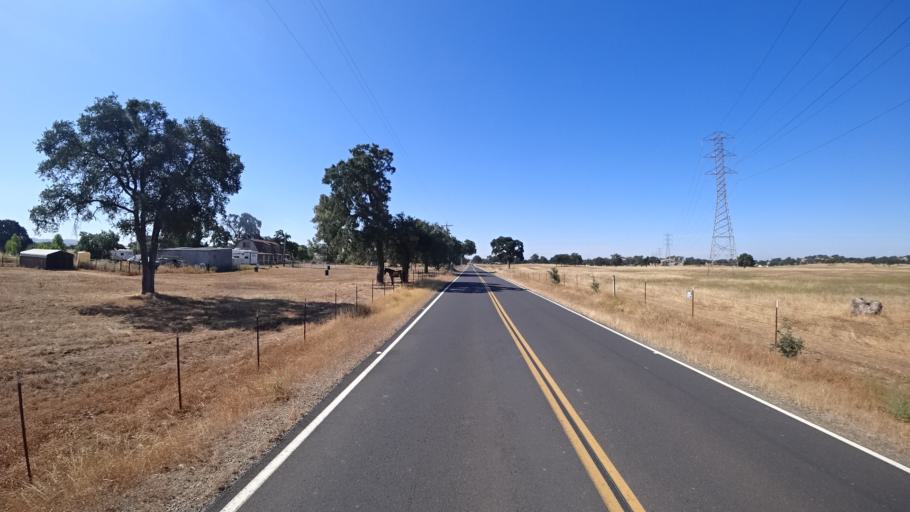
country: US
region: California
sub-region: Calaveras County
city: Rancho Calaveras
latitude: 38.1030
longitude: -120.9086
